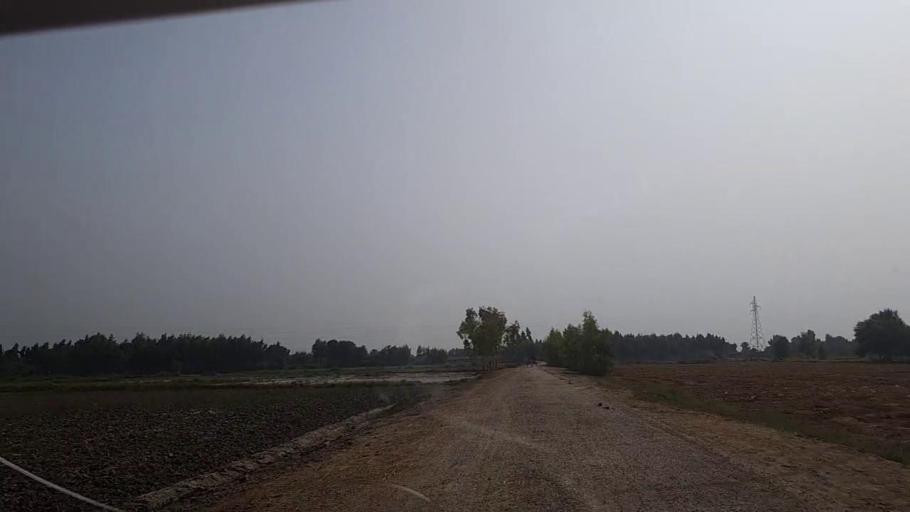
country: PK
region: Sindh
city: Madeji
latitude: 27.7369
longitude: 68.4357
